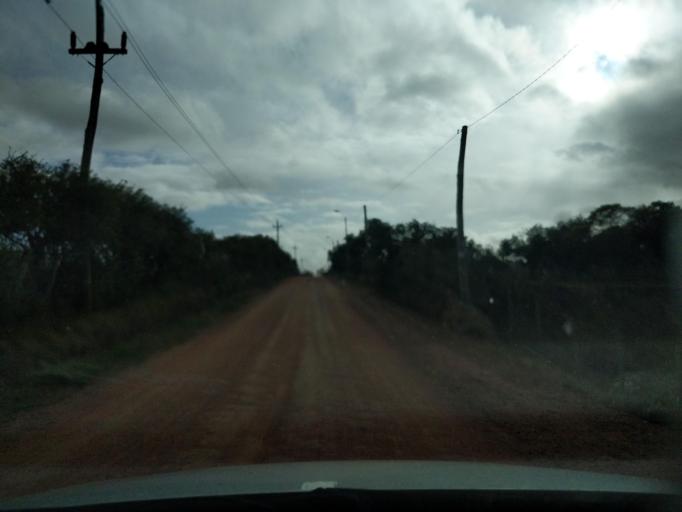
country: UY
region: Florida
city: Florida
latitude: -34.0646
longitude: -56.2181
